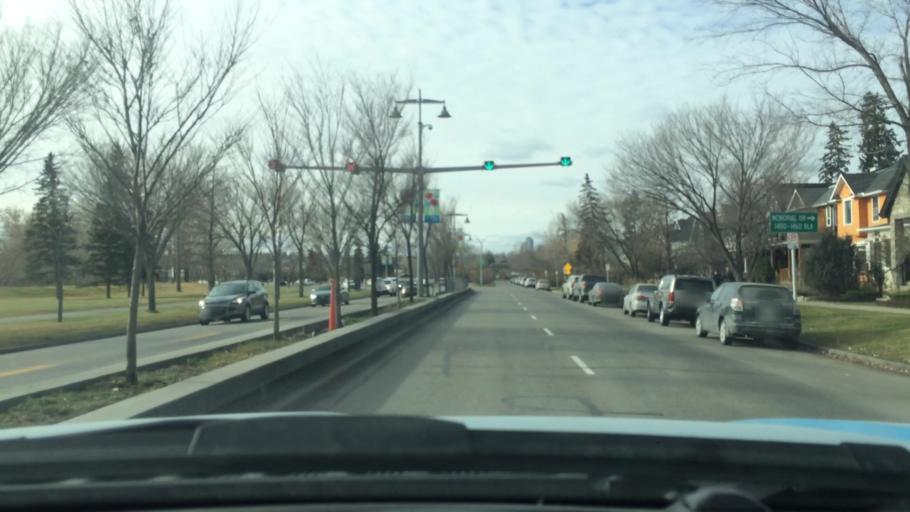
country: CA
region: Alberta
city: Calgary
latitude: 51.0511
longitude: -114.0899
